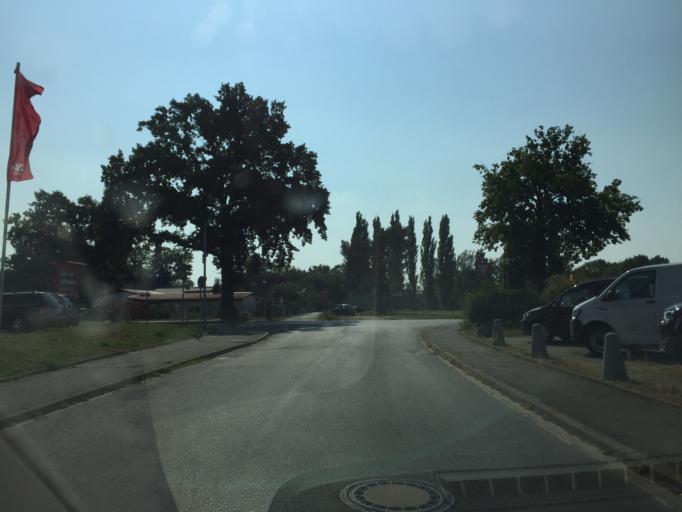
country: DE
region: Brandenburg
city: Erkner
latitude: 52.4286
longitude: 13.7418
